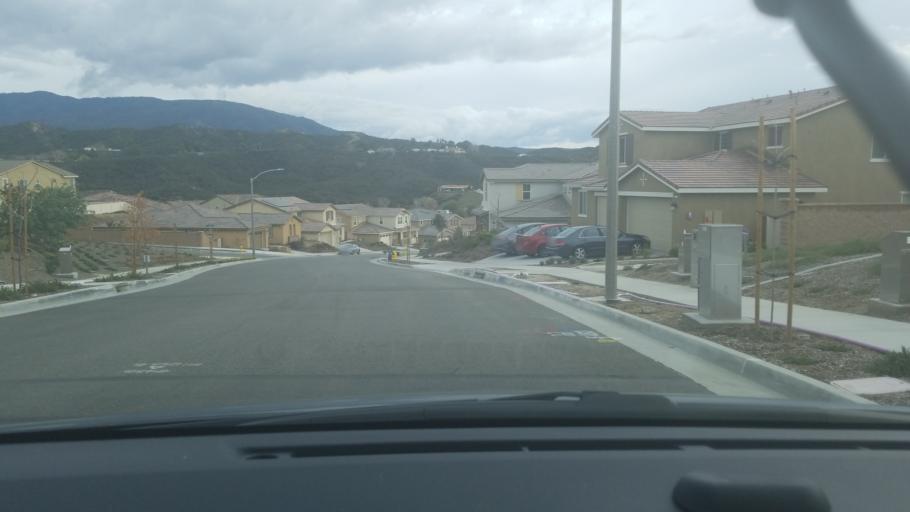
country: US
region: California
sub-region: Riverside County
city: Temecula
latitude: 33.4664
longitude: -117.0798
